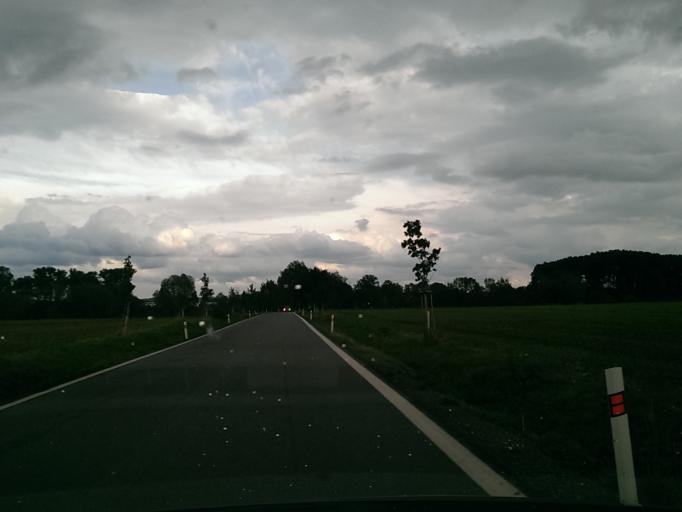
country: CZ
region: Central Bohemia
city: Bakov nad Jizerou
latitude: 50.4833
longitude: 14.9789
